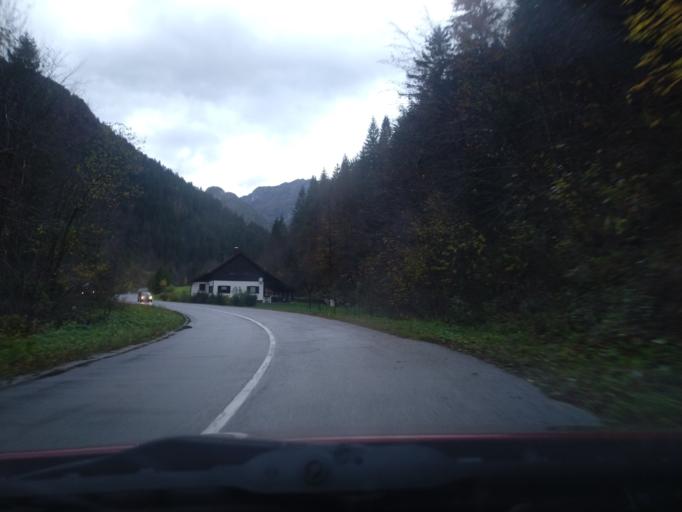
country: SI
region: Solcava
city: Solcava
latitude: 46.4036
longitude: 14.7048
